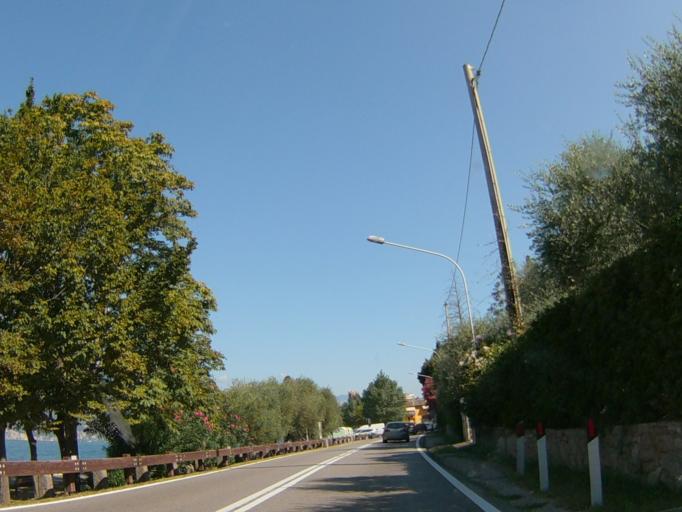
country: IT
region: Veneto
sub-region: Provincia di Verona
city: San Zeno di Montagna
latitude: 45.6526
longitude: 10.7222
